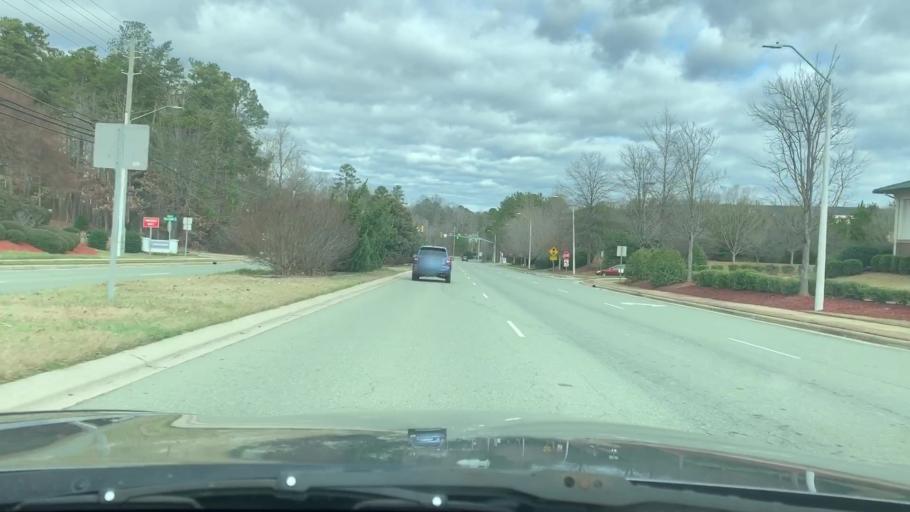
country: US
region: North Carolina
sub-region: Wake County
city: Cary
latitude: 35.8043
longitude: -78.7829
